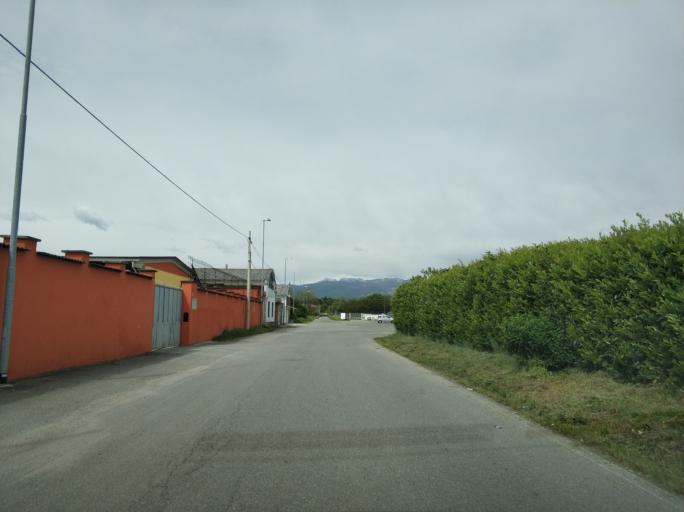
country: IT
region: Piedmont
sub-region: Provincia di Torino
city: Caselle Torinese
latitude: 45.1655
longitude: 7.6496
